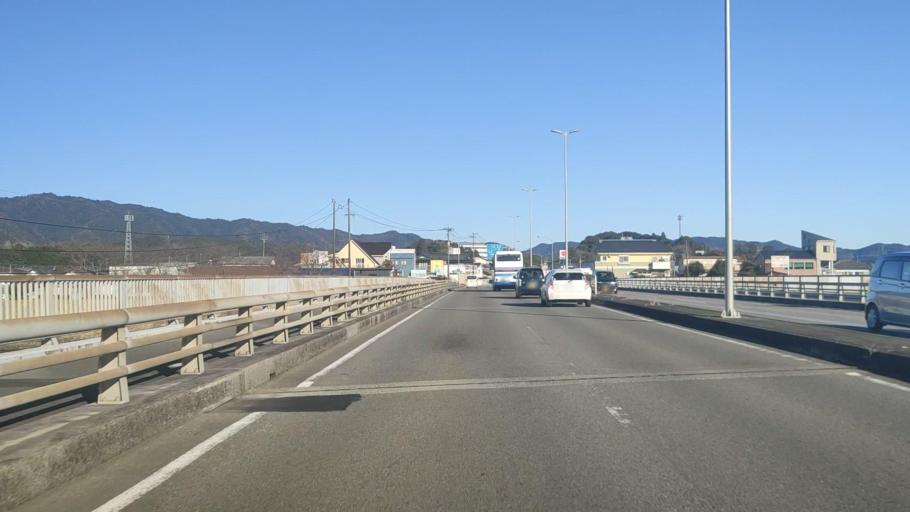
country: JP
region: Miyazaki
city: Nobeoka
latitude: 32.4642
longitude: 131.6486
